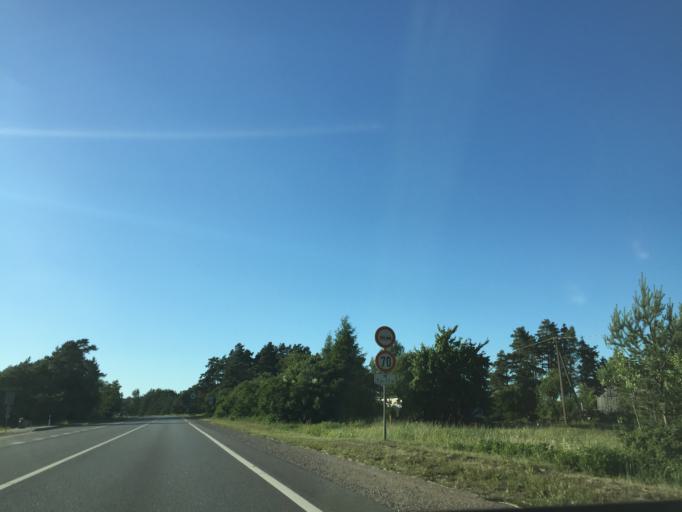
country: LV
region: Ventspils
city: Ventspils
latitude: 57.3960
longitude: 21.6959
